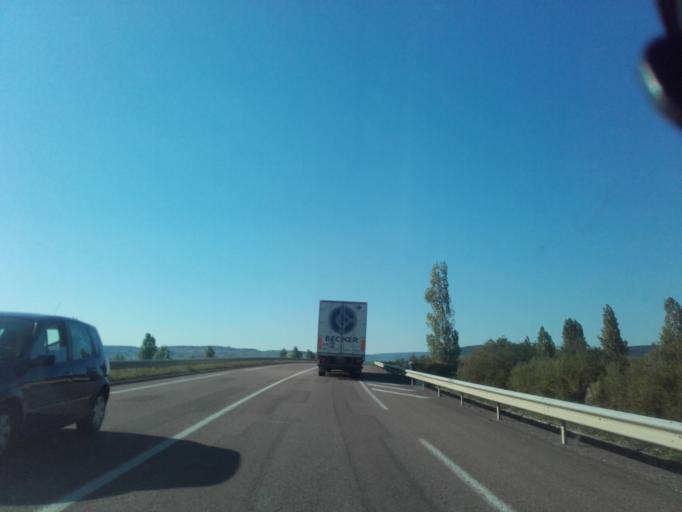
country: FR
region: Bourgogne
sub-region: Departement de la Cote-d'Or
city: Bligny-les-Beaune
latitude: 47.0033
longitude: 4.8321
